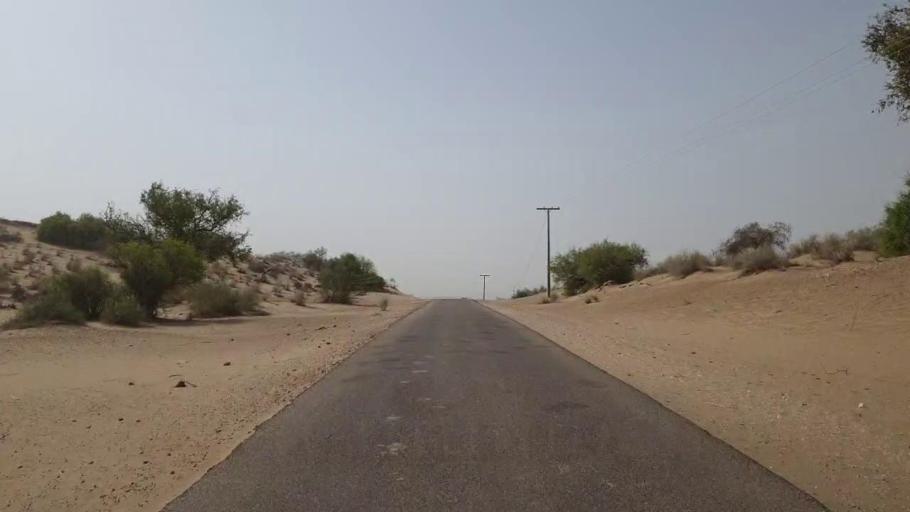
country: PK
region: Sindh
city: Mithi
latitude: 24.5989
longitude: 69.9243
